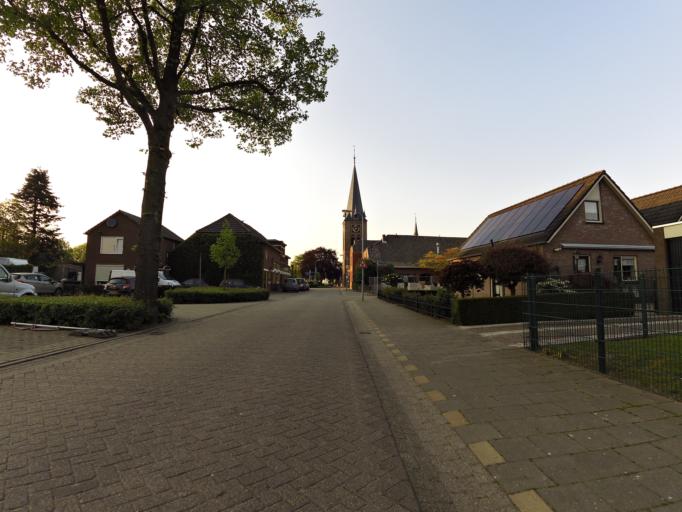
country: NL
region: Gelderland
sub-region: Gemeente Montferland
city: s-Heerenberg
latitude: 51.8555
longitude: 6.3126
